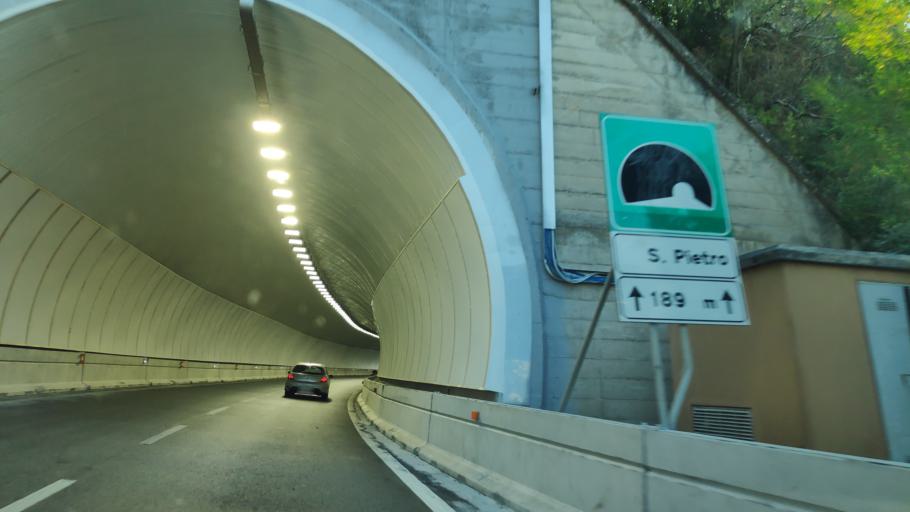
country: IT
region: Calabria
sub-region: Provincia di Cosenza
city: Belsito
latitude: 39.1753
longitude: 16.2941
